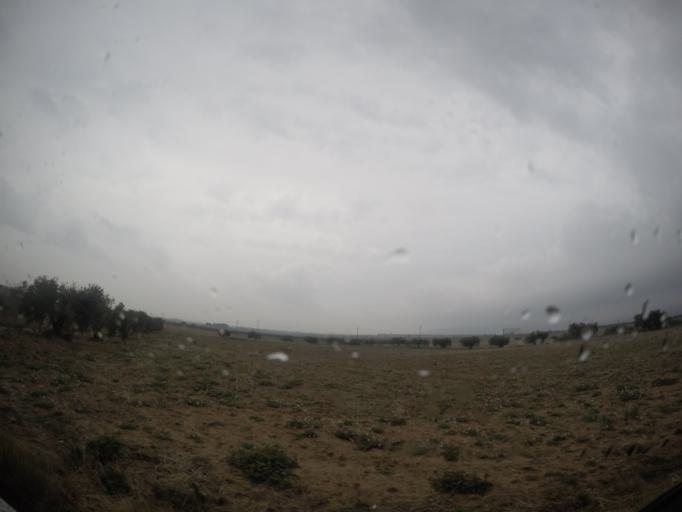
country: ES
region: Catalonia
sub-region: Provincia de Tarragona
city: la Bisbal del Penedes
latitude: 41.2817
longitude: 1.5148
